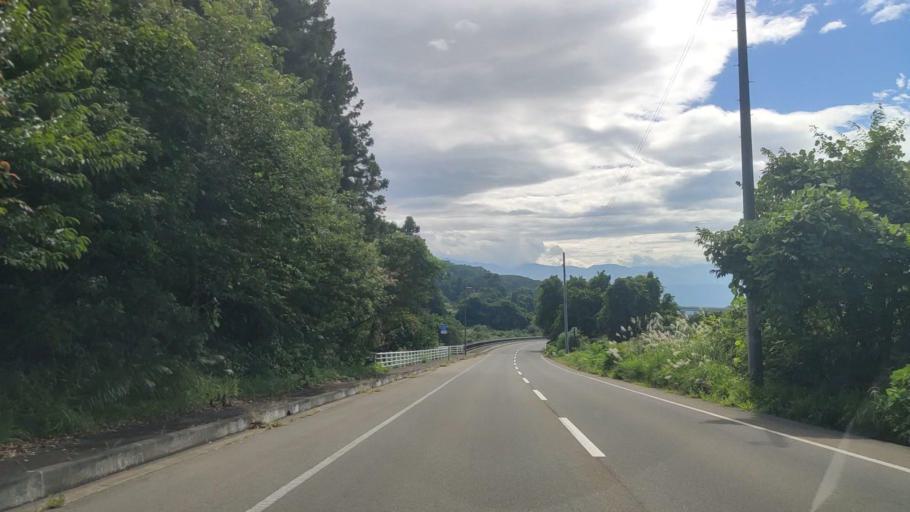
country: JP
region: Nagano
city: Nakano
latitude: 36.7919
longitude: 138.3165
